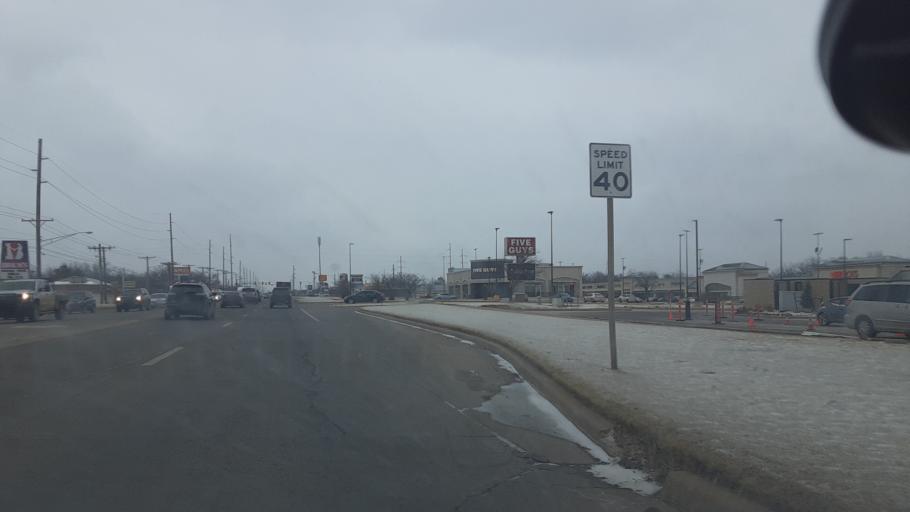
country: US
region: Oklahoma
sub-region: Payne County
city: Stillwater
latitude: 36.1272
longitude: -97.0513
